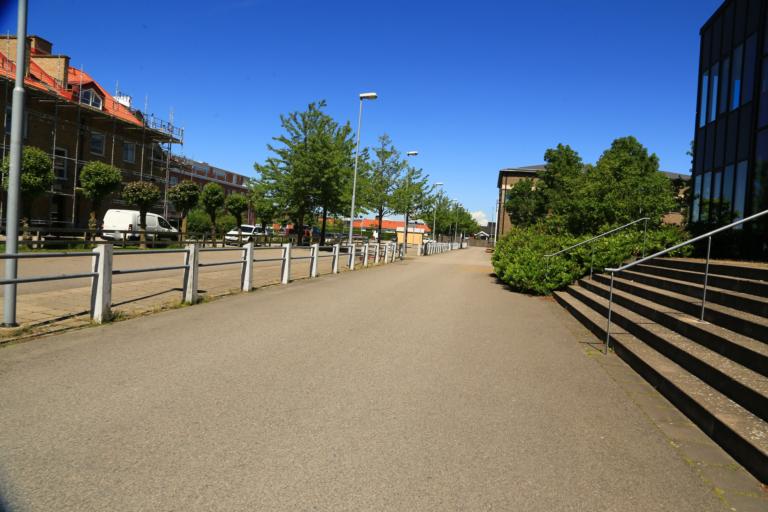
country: SE
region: Halland
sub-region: Varbergs Kommun
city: Varberg
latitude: 57.1058
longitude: 12.2702
